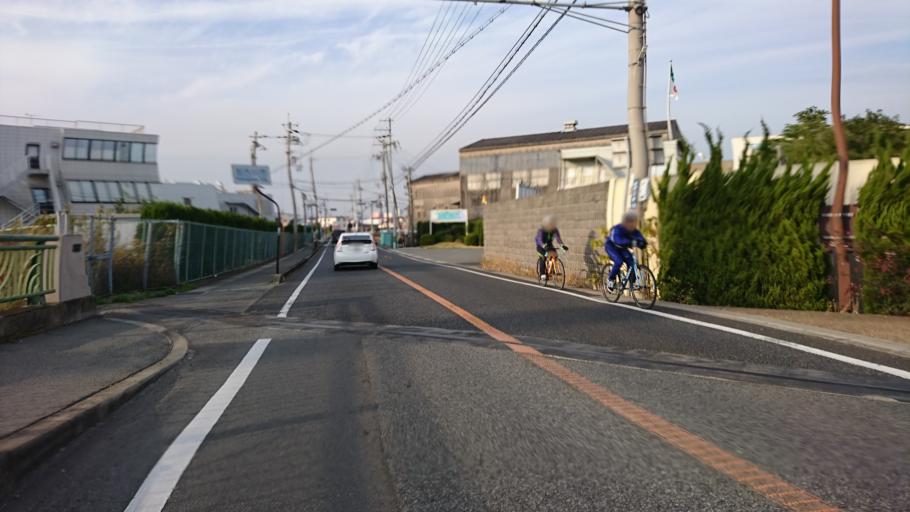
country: JP
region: Hyogo
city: Kakogawacho-honmachi
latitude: 34.7217
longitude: 134.8514
